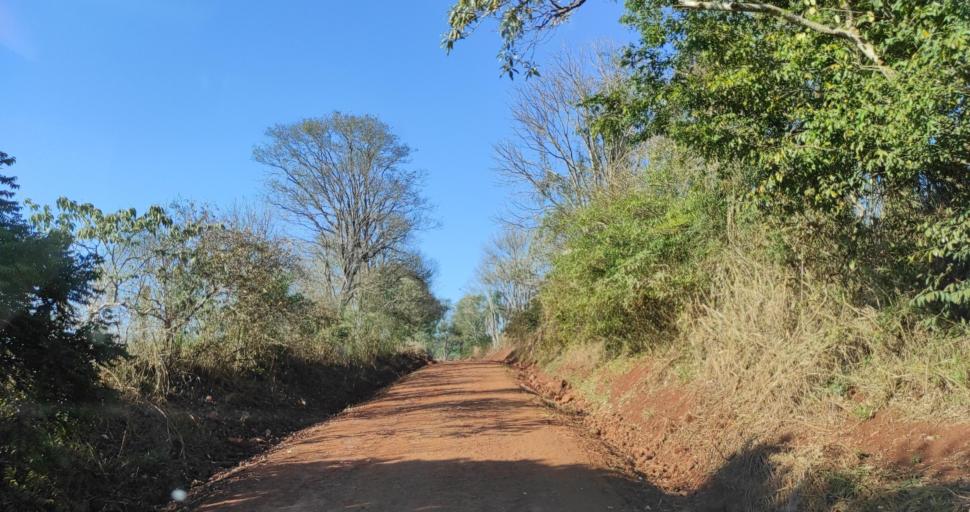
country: AR
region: Misiones
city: Capiovi
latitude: -26.8668
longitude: -55.0431
